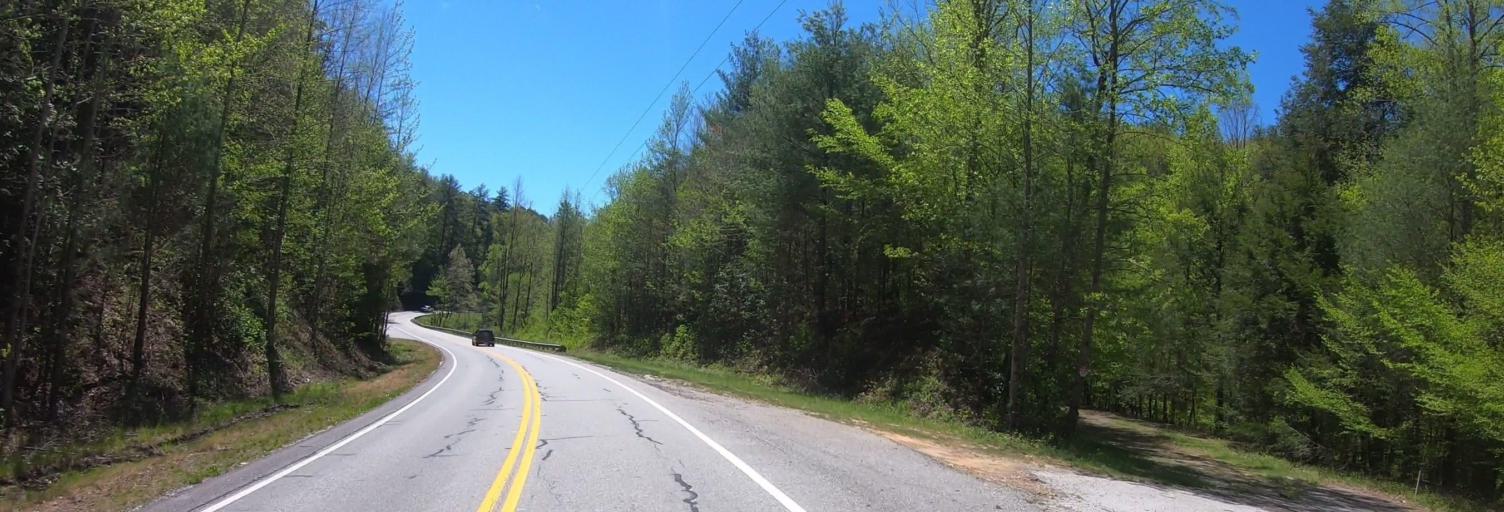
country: US
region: Georgia
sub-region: White County
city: Cleveland
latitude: 34.7215
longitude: -83.7477
